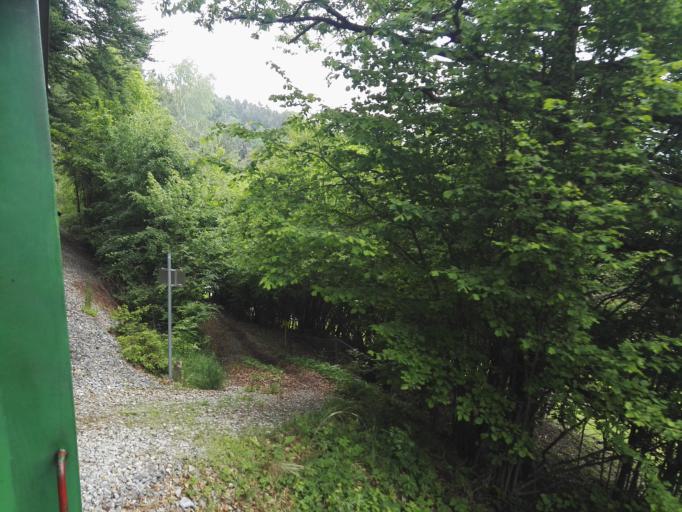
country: AT
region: Styria
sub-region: Politischer Bezirk Weiz
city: Puch bei Weiz
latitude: 47.2318
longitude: 15.6776
